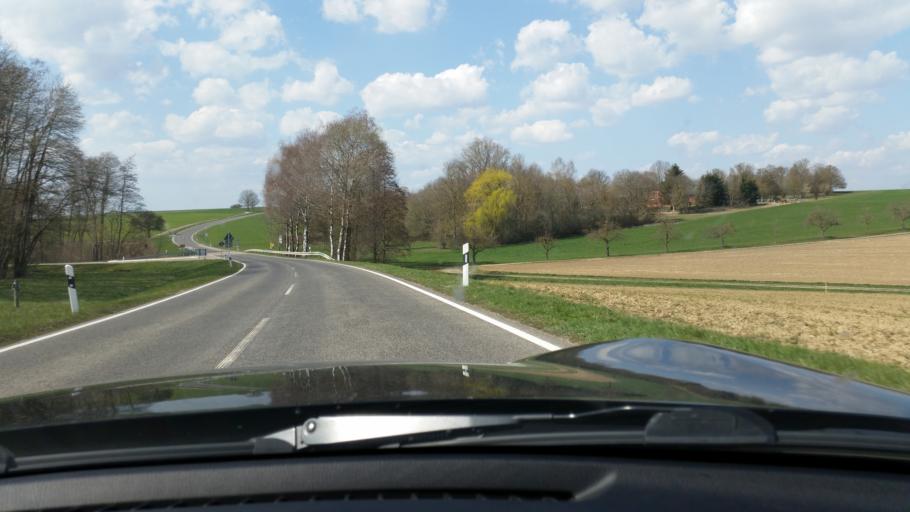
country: DE
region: Baden-Wuerttemberg
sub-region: Regierungsbezirk Stuttgart
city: Langenburg
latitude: 49.2679
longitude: 9.8055
